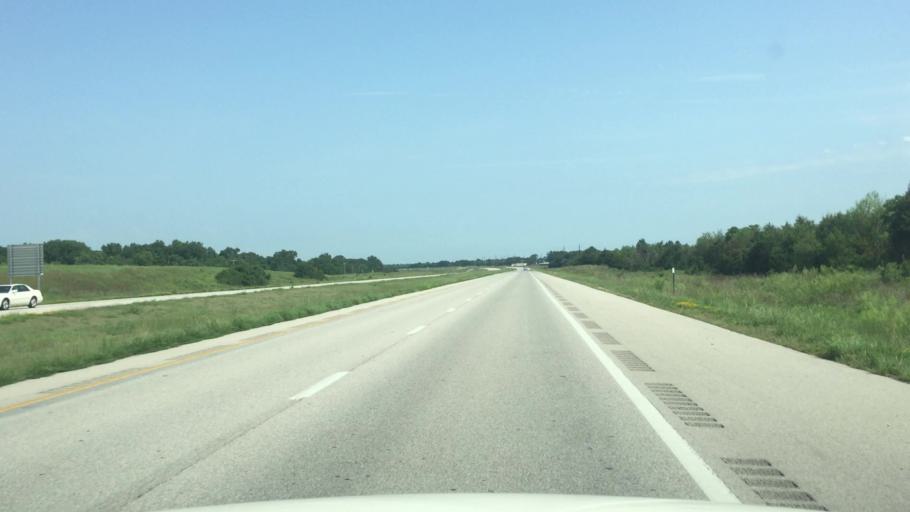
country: US
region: Kansas
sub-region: Montgomery County
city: Coffeyville
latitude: 37.0569
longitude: -95.5817
